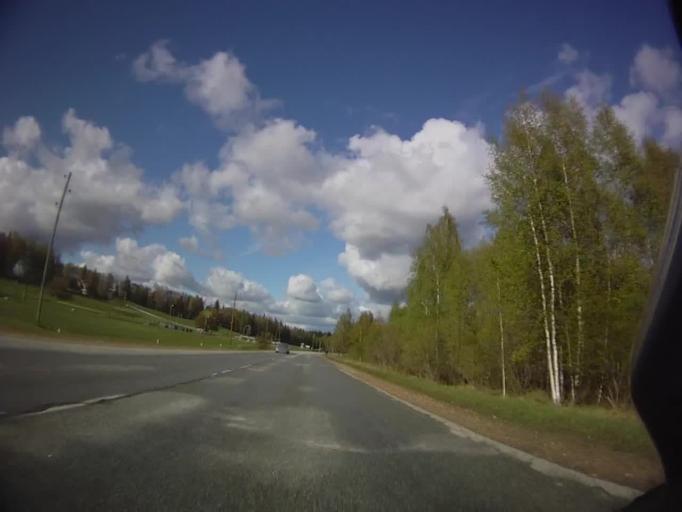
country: LV
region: Sigulda
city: Sigulda
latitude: 57.1767
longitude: 24.8190
